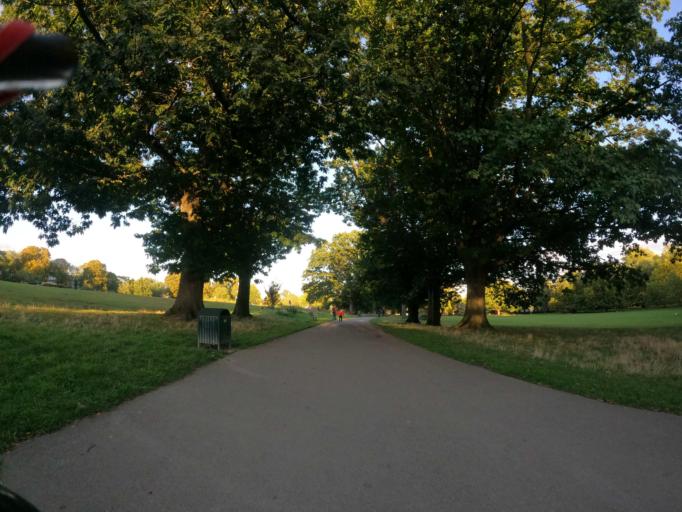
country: GB
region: England
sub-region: Greater London
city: Acton
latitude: 51.5081
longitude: -0.2599
